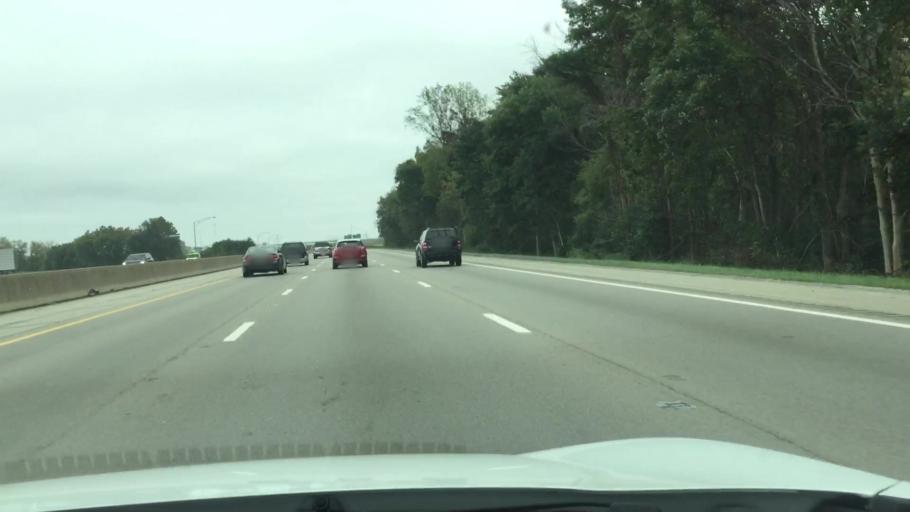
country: US
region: Ohio
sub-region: Clark County
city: Crystal Lakes
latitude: 39.8644
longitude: -84.0066
